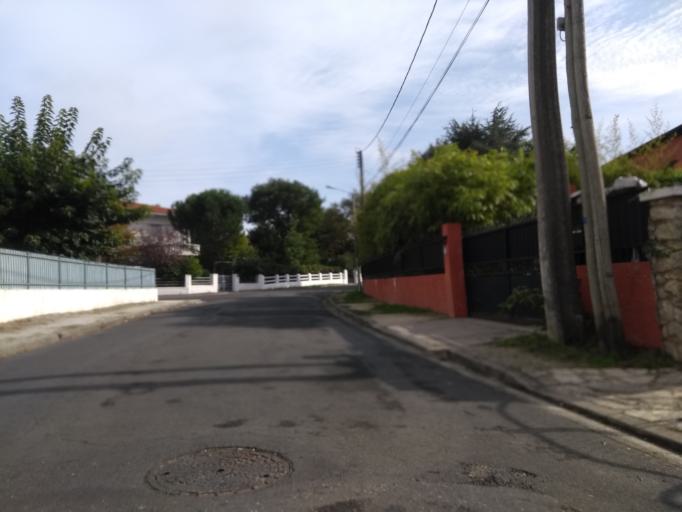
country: FR
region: Aquitaine
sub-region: Departement de la Gironde
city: Merignac
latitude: 44.8148
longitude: -0.6175
